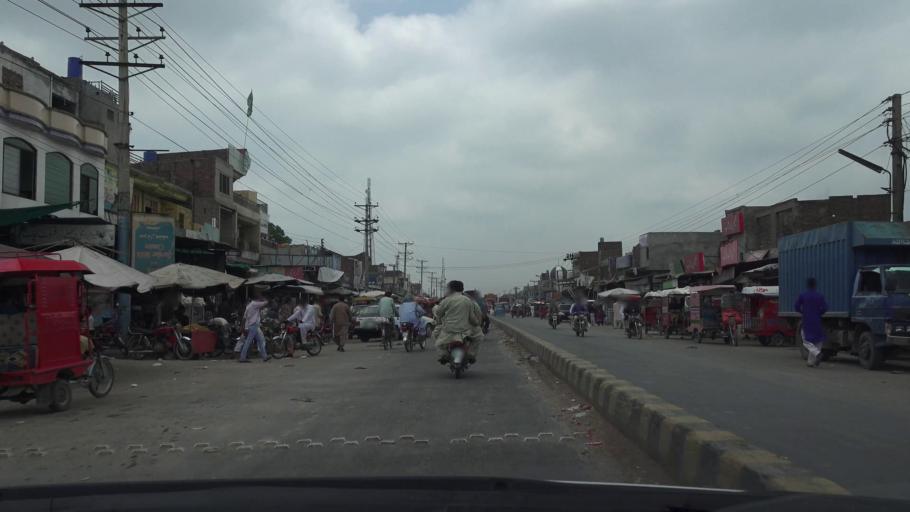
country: PK
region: Punjab
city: Faisalabad
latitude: 31.3886
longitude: 73.1964
